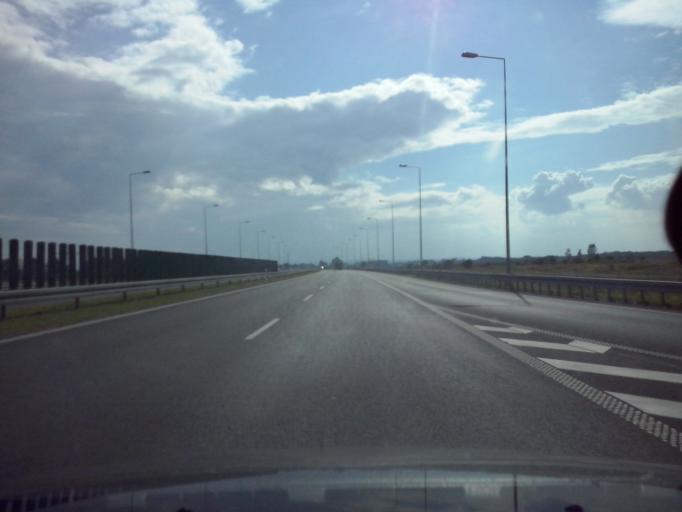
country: PL
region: Lesser Poland Voivodeship
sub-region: Powiat tarnowski
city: Wierzchoslawice
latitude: 50.0399
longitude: 20.8873
